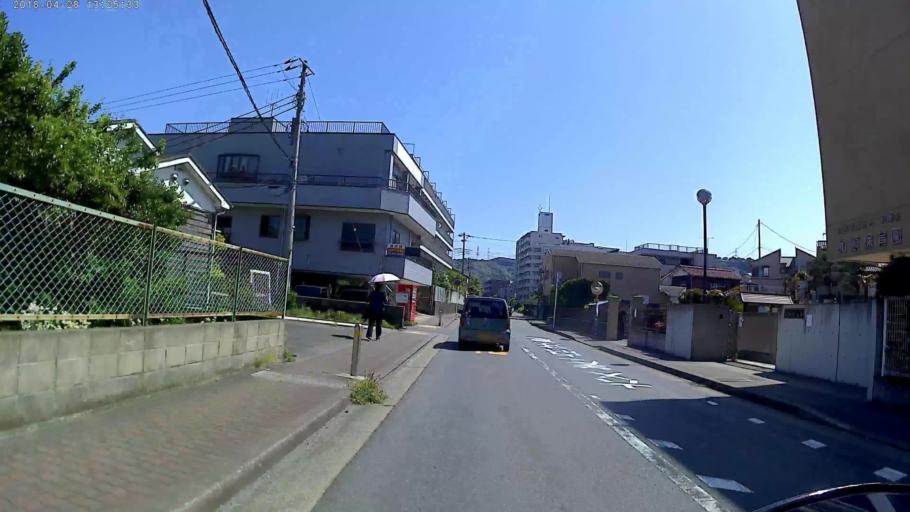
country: JP
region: Kanagawa
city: Yokosuka
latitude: 35.2313
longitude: 139.6974
